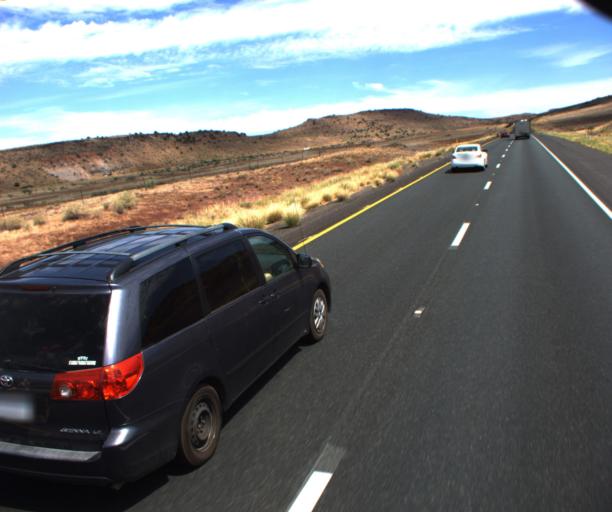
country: US
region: Arizona
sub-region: Yavapai County
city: Cordes Lakes
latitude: 34.4455
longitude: -112.0308
